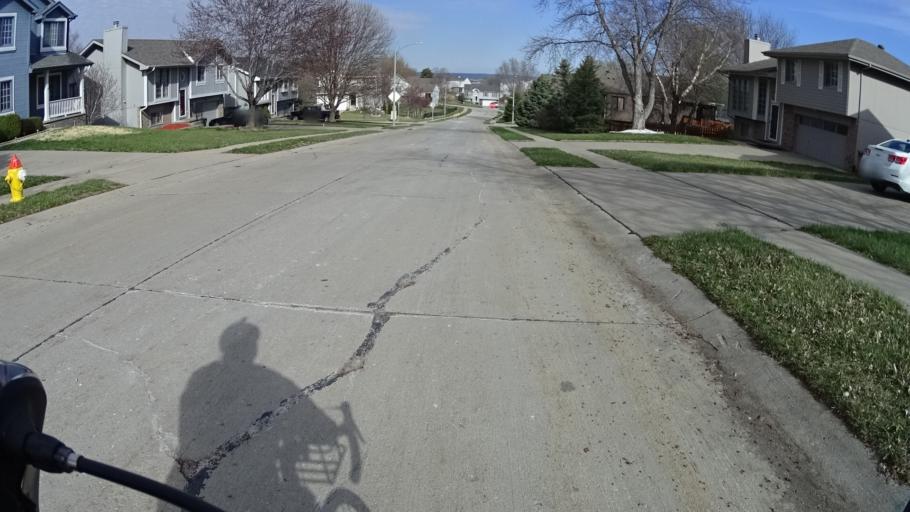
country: US
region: Nebraska
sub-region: Sarpy County
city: Offutt Air Force Base
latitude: 41.1098
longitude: -95.9621
